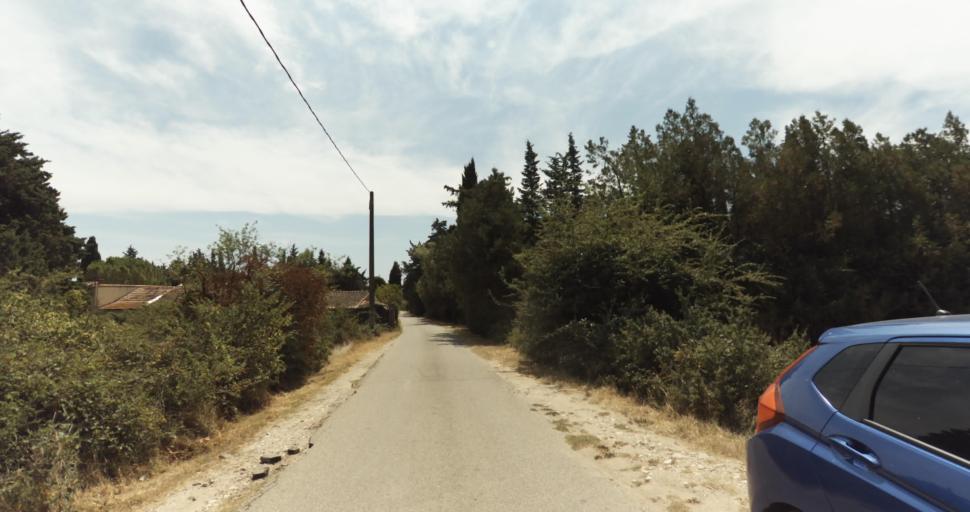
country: FR
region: Provence-Alpes-Cote d'Azur
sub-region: Departement du Vaucluse
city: Monteux
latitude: 44.0540
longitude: 4.9957
